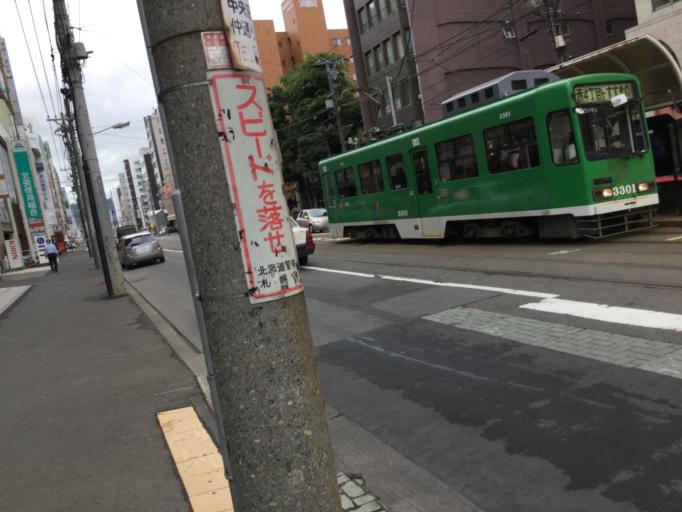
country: JP
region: Hokkaido
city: Sapporo
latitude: 43.0580
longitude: 141.3462
